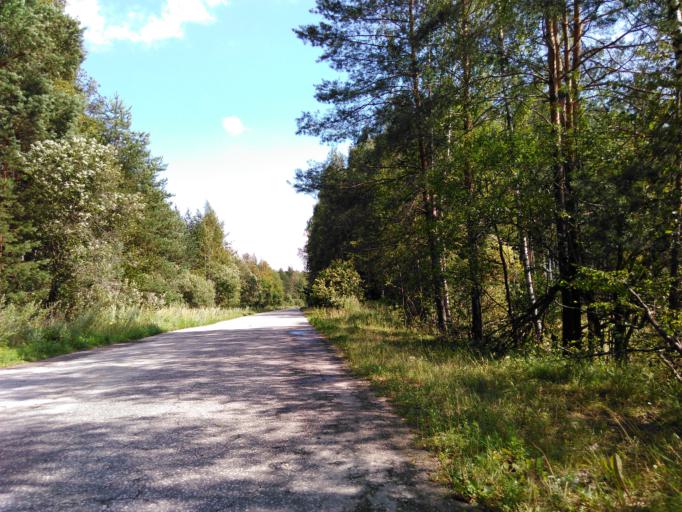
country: RU
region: Vladimir
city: Krasnyy Oktyabr'
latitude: 56.0241
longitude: 38.7842
